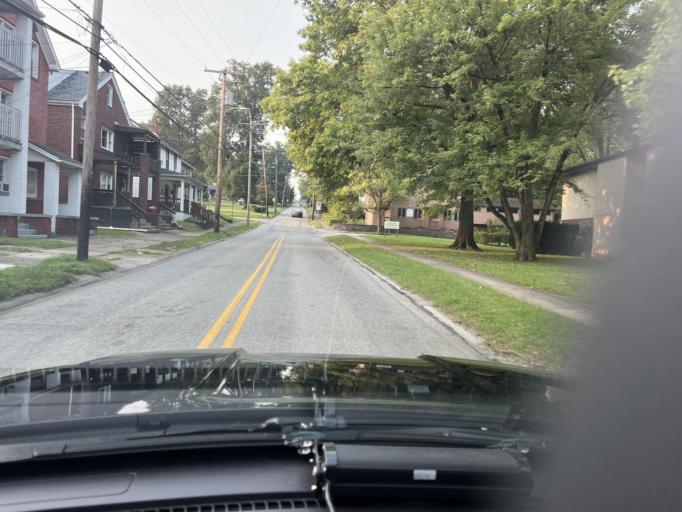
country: US
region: Pennsylvania
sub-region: Fayette County
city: Uniontown
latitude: 39.8914
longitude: -79.7255
